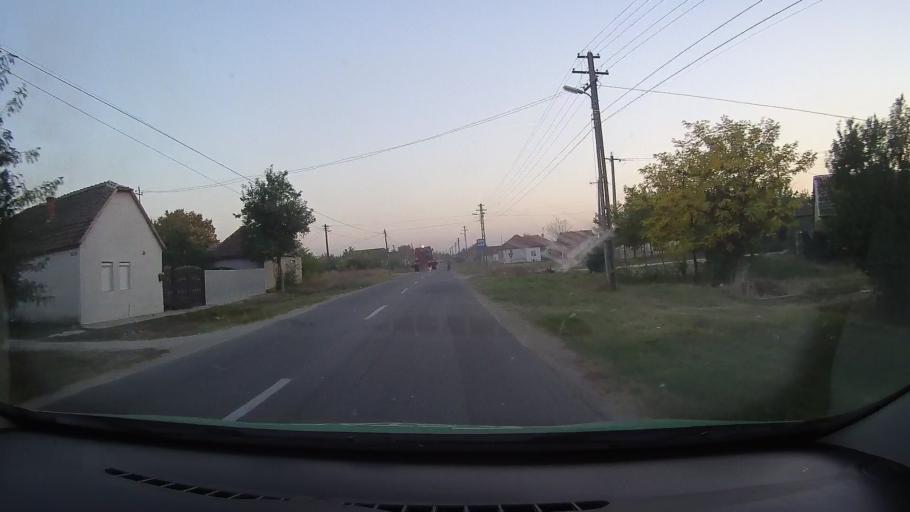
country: RO
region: Arad
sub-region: Comuna Santana
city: Santana
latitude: 46.3602
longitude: 21.5198
